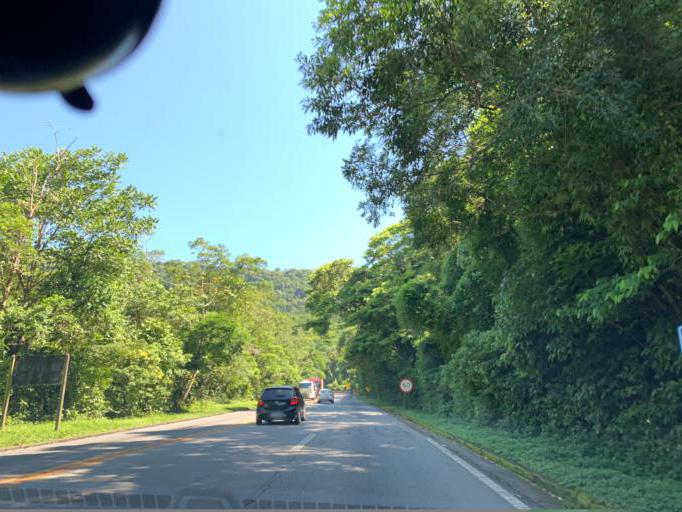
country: BR
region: Sao Paulo
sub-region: Bertioga
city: Bertioga
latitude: -23.7519
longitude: -46.0393
